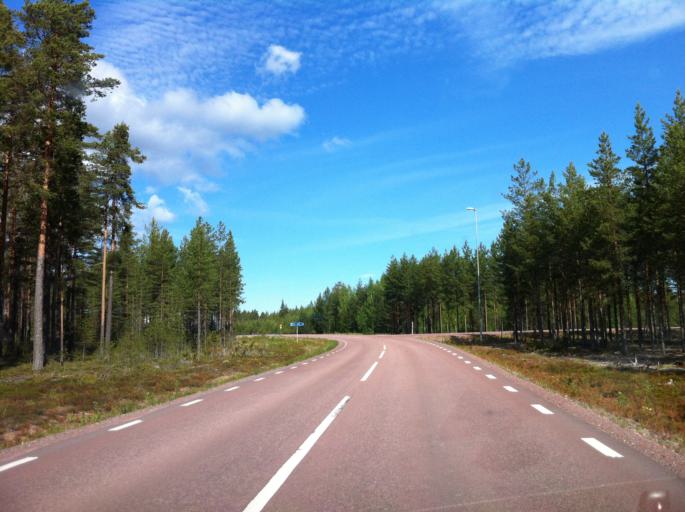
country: SE
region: Dalarna
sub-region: Mora Kommun
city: Mora
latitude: 60.9647
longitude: 14.5201
